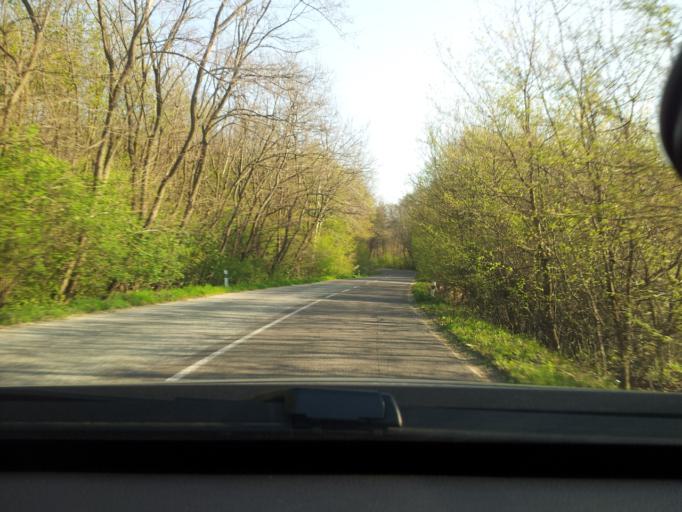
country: SK
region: Nitriansky
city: Tlmace
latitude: 48.2965
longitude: 18.4502
